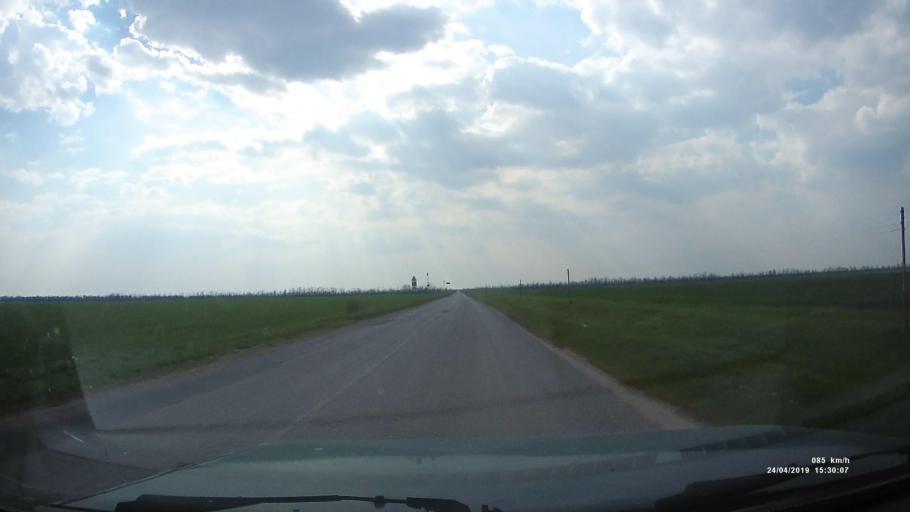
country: RU
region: Rostov
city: Remontnoye
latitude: 46.5999
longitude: 43.0128
